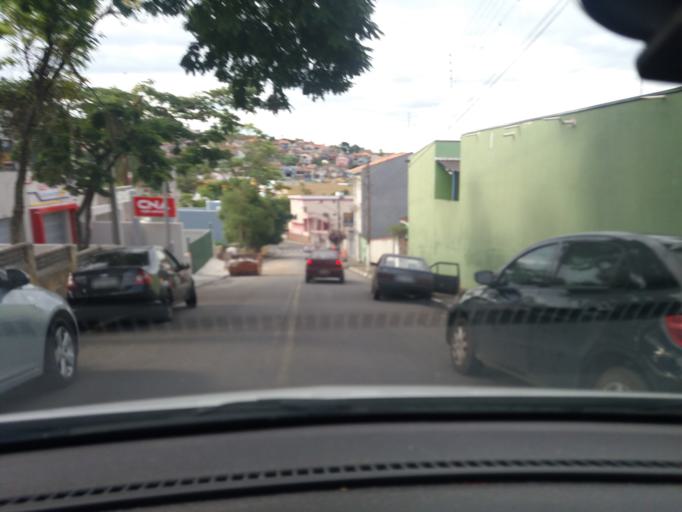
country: BR
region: Sao Paulo
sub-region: Bom Jesus Dos Perdoes
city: Bom Jesus dos Perdoes
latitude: -23.1340
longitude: -46.4660
